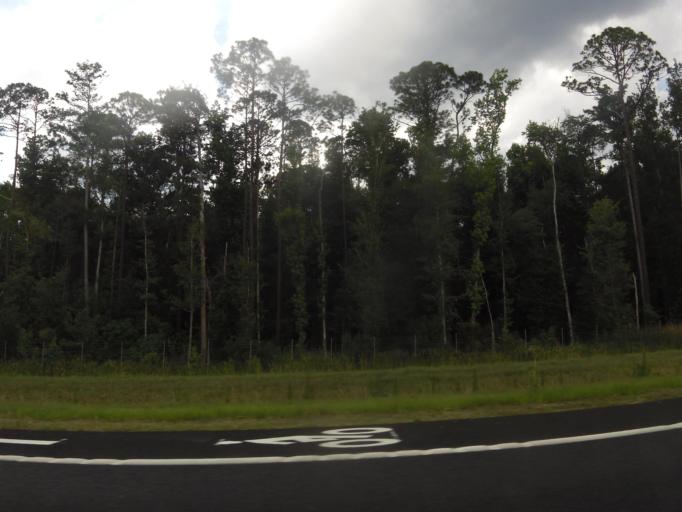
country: US
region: Florida
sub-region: Duval County
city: Baldwin
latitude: 30.3212
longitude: -81.9716
